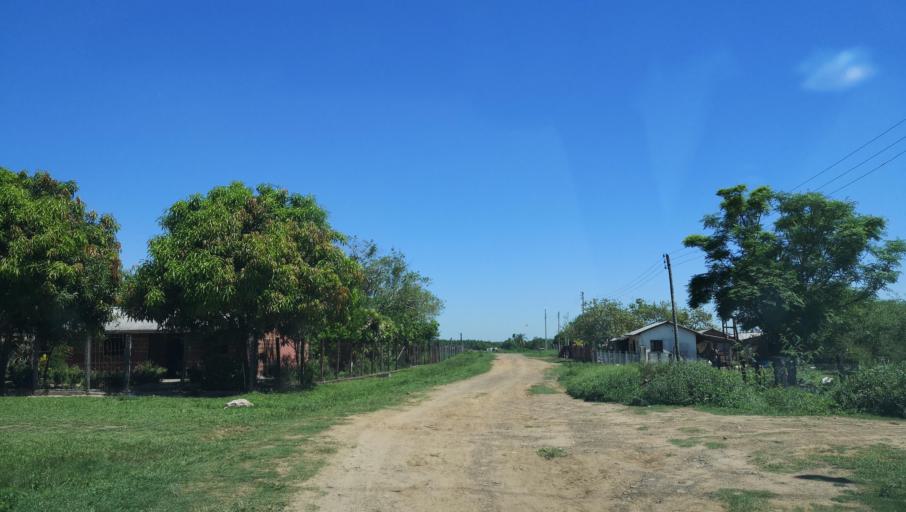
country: PY
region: Caaguazu
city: Carayao
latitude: -25.1921
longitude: -56.4036
